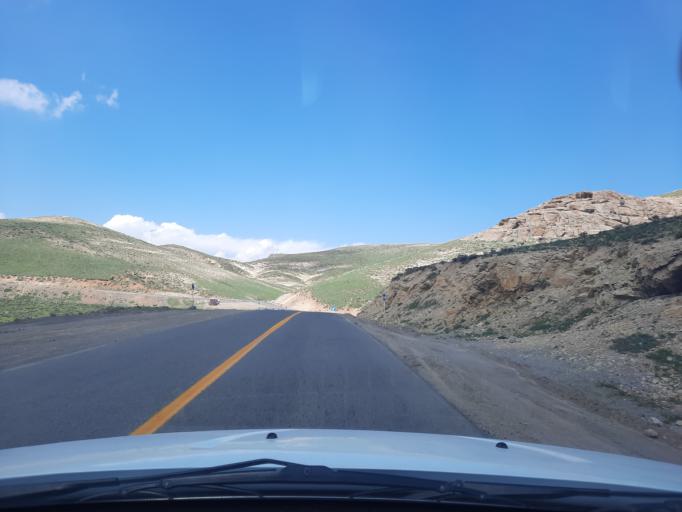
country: IR
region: Qazvin
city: Qazvin
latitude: 36.3869
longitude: 50.2114
